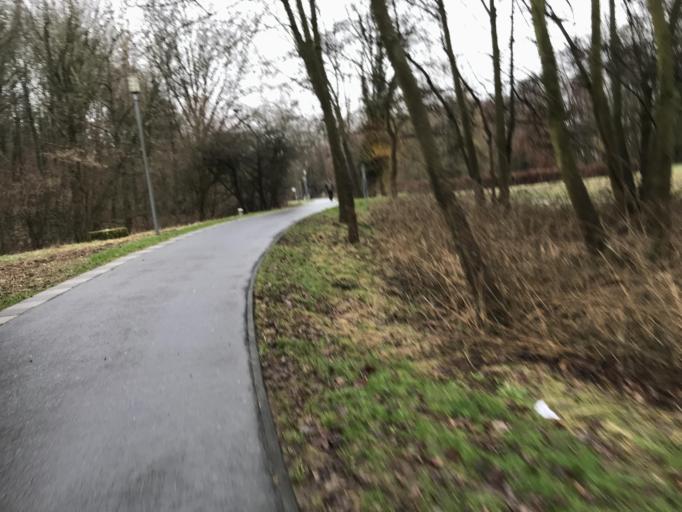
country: DE
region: Hesse
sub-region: Regierungsbezirk Kassel
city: Bad Wildungen
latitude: 51.1227
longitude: 9.1271
